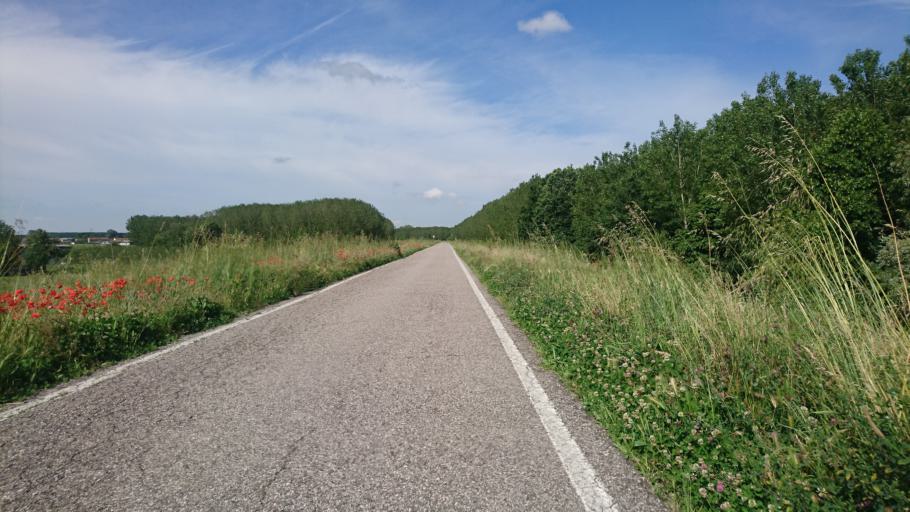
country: IT
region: Veneto
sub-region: Provincia di Rovigo
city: Melara
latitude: 45.0511
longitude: 11.1911
